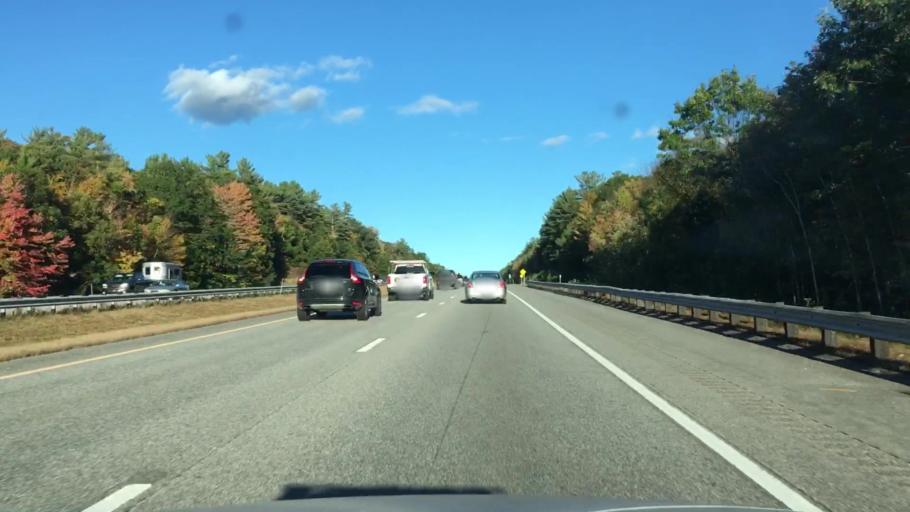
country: US
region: New Hampshire
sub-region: Rockingham County
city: Auburn
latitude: 43.0304
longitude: -71.3544
